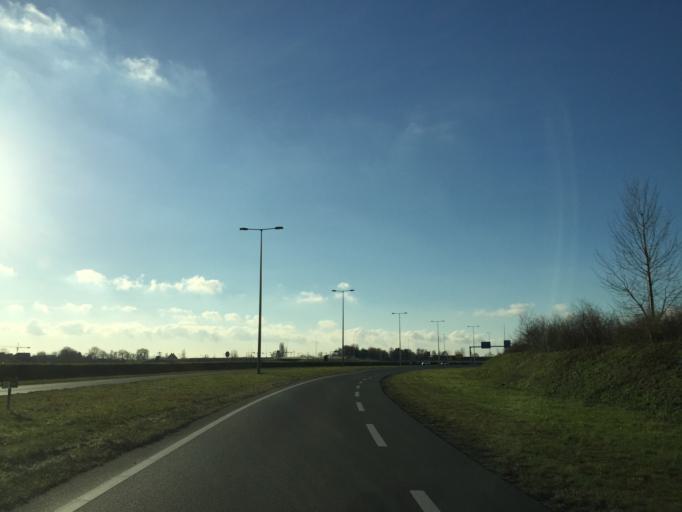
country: NL
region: South Holland
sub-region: Gemeente Lansingerland
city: Berkel en Rodenrijs
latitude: 52.0028
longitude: 4.4556
